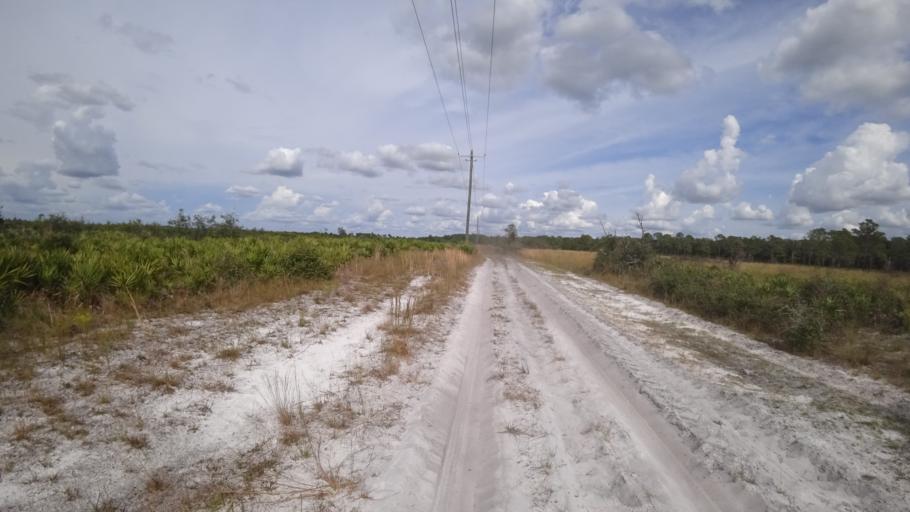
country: US
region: Florida
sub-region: Hillsborough County
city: Wimauma
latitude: 27.5410
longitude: -82.1405
